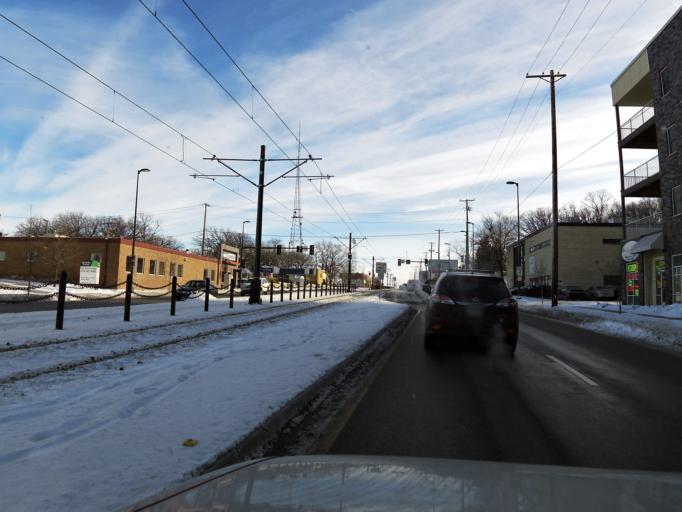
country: US
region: Minnesota
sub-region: Ramsey County
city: Lauderdale
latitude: 44.9703
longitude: -93.2137
